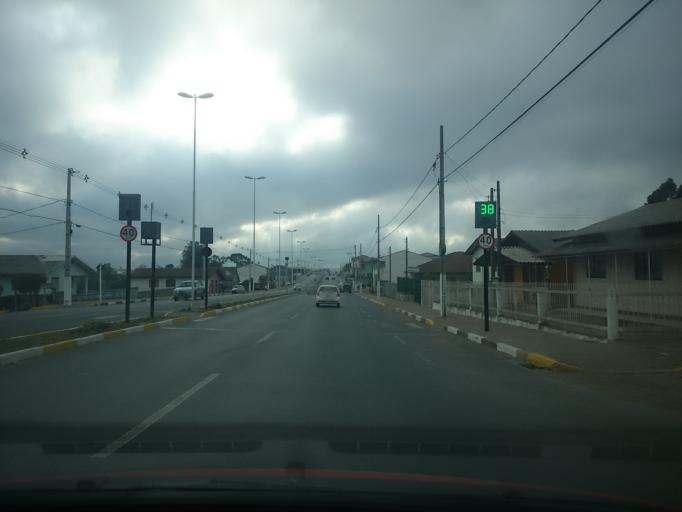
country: BR
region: Santa Catarina
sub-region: Lages
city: Lages
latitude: -27.8314
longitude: -50.3446
